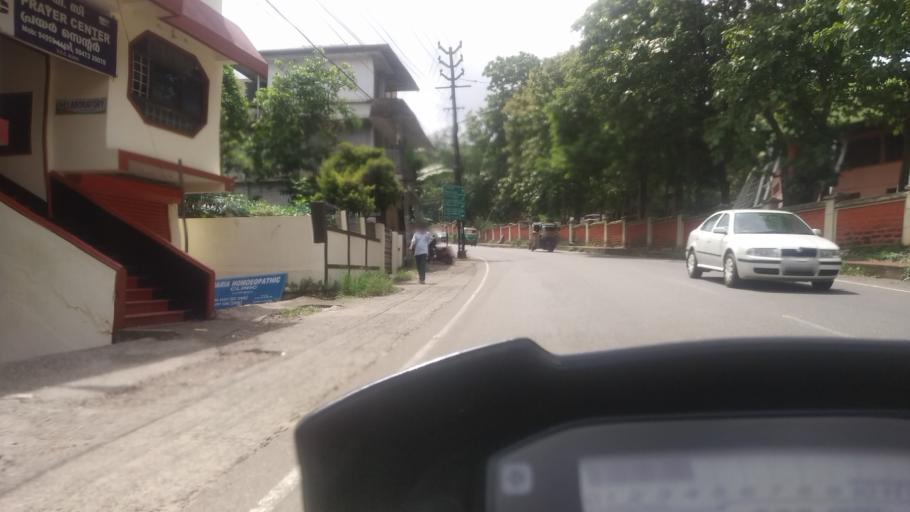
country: IN
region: Kerala
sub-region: Ernakulam
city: Aluva
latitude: 10.1239
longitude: 76.3349
